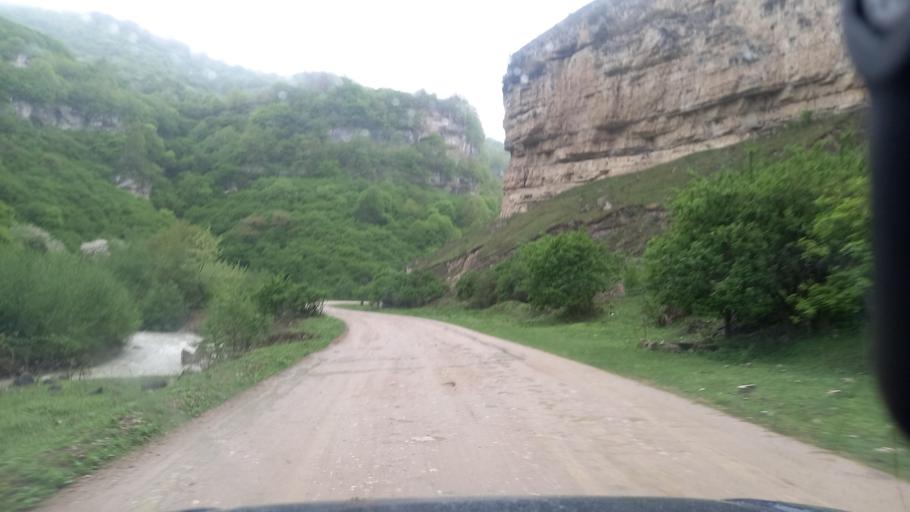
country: RU
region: Kabardino-Balkariya
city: Gundelen
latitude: 43.5967
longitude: 43.1423
